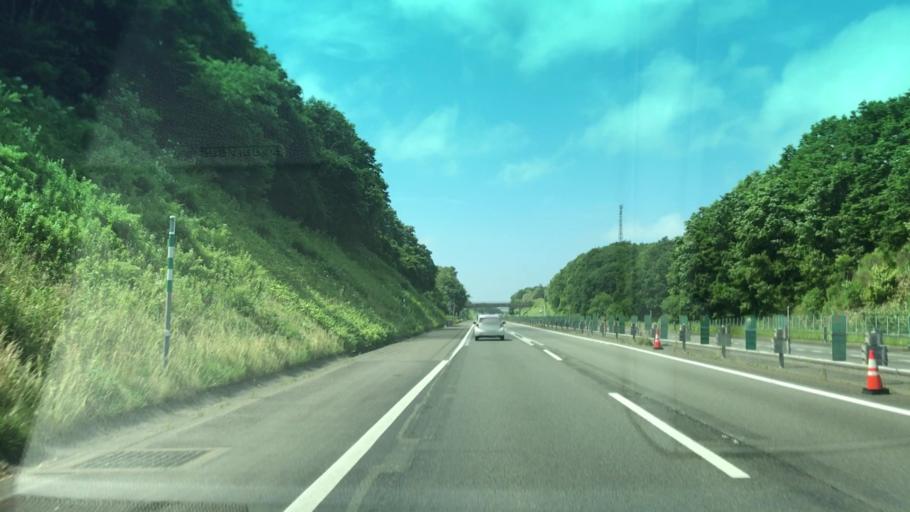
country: JP
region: Hokkaido
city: Kitahiroshima
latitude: 42.9291
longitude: 141.5343
